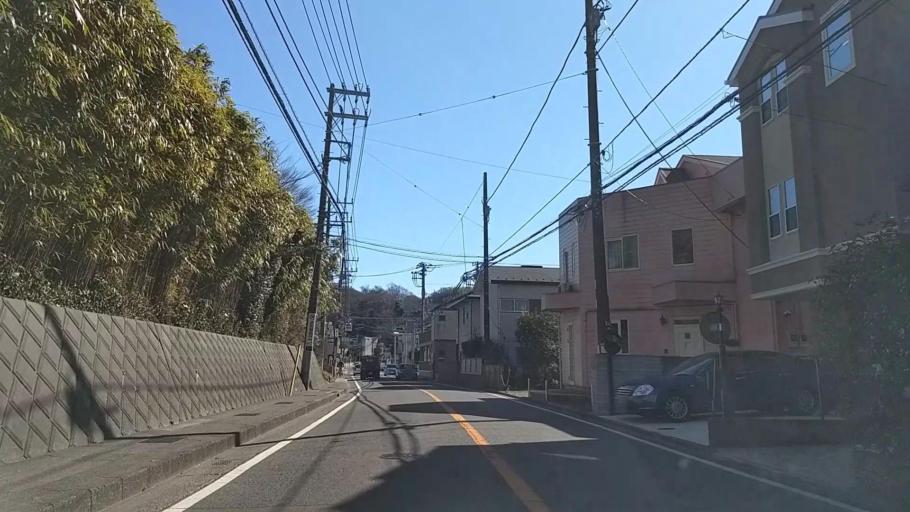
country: JP
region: Kanagawa
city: Kamakura
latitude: 35.3226
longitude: 139.5260
